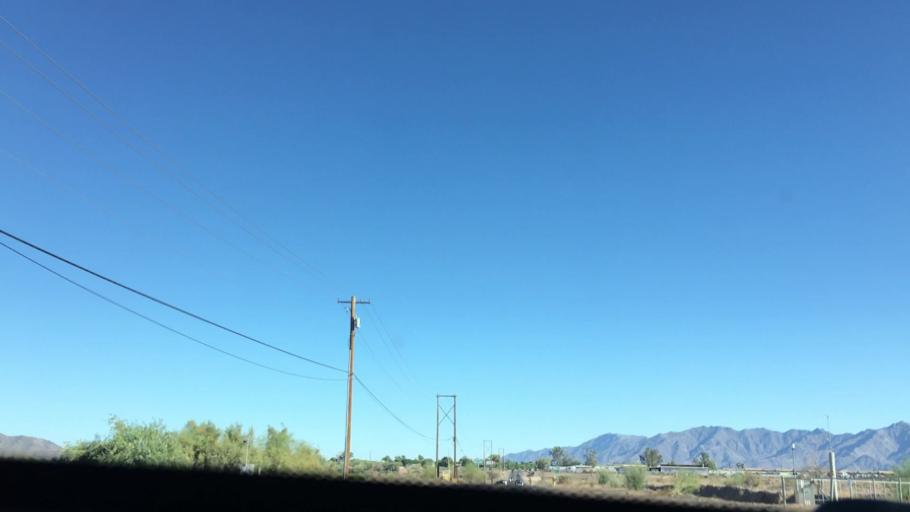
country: US
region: Arizona
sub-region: Maricopa County
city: Laveen
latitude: 33.3989
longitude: -112.2041
